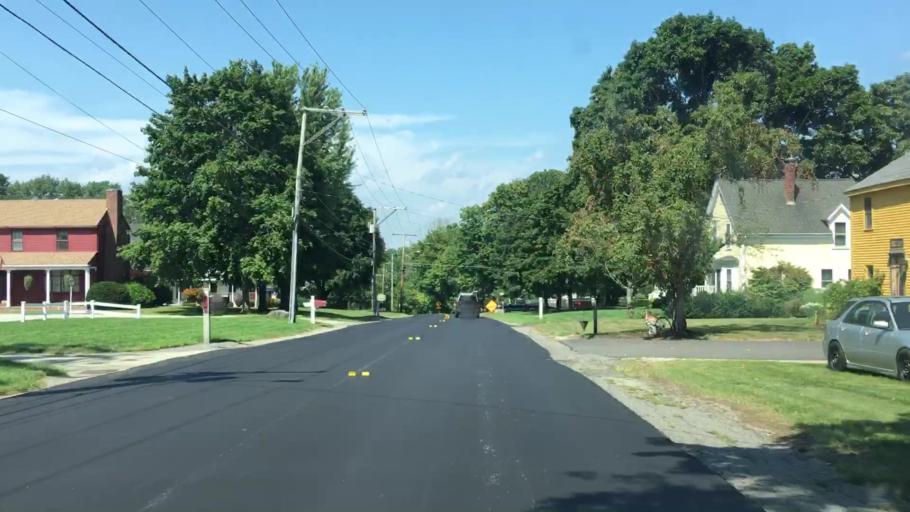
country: US
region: New Hampshire
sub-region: Rockingham County
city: Hampstead
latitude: 42.8814
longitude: -71.1868
